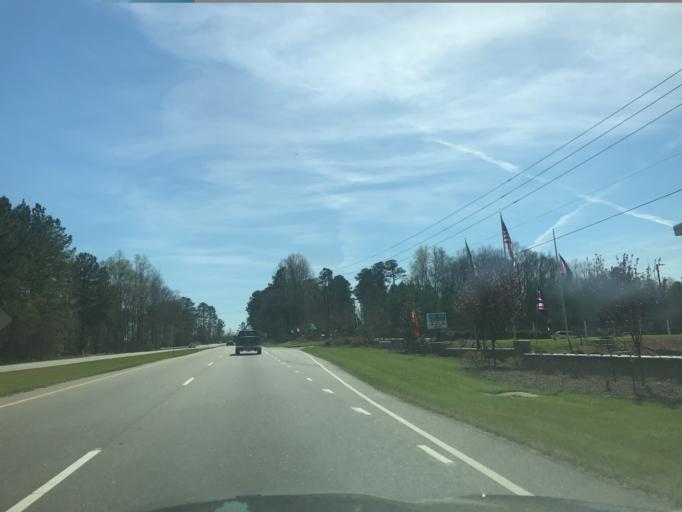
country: US
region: North Carolina
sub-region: Wake County
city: Garner
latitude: 35.6823
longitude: -78.6859
